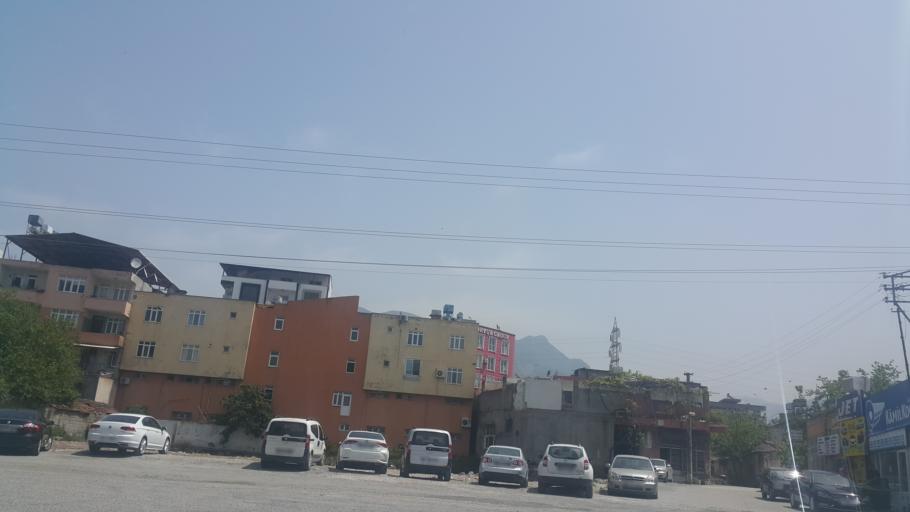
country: TR
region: Hatay
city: Yakacik
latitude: 36.7553
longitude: 36.2154
